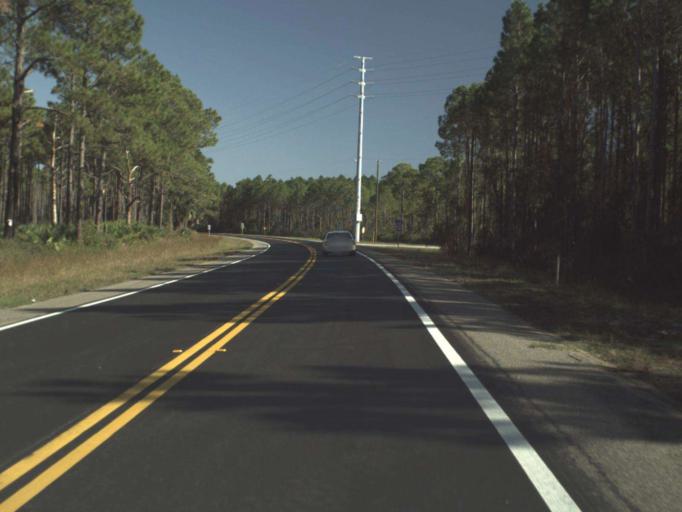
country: US
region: Florida
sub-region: Franklin County
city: Apalachicola
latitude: 29.7207
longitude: -85.1089
